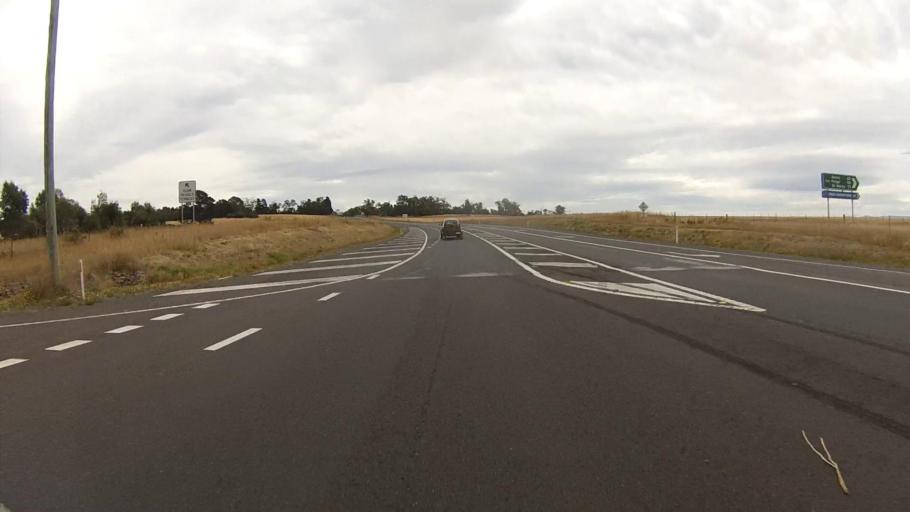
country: AU
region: Tasmania
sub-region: Northern Midlands
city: Evandale
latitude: -41.8363
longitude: 147.4476
